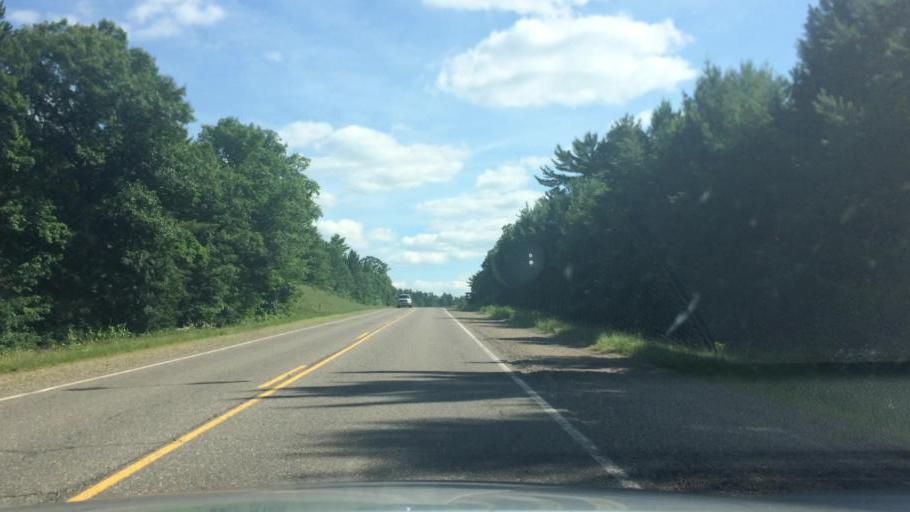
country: US
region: Wisconsin
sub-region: Vilas County
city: Lac du Flambeau
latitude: 46.0446
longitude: -89.6497
